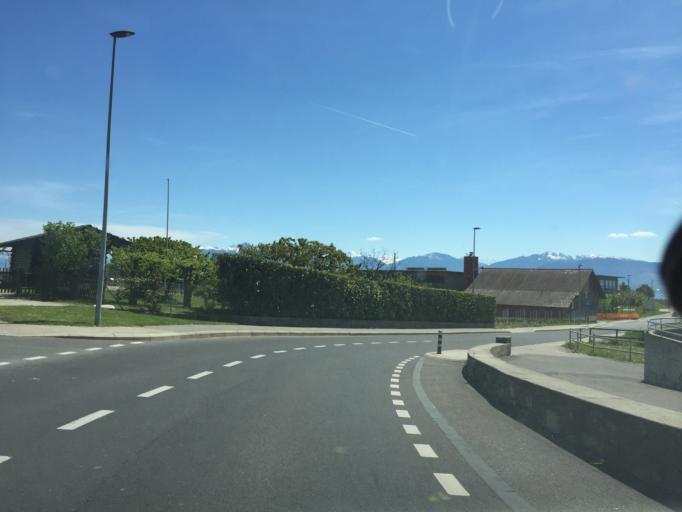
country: CH
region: Vaud
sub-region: Morges District
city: Aubonne
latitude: 46.4844
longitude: 6.4217
